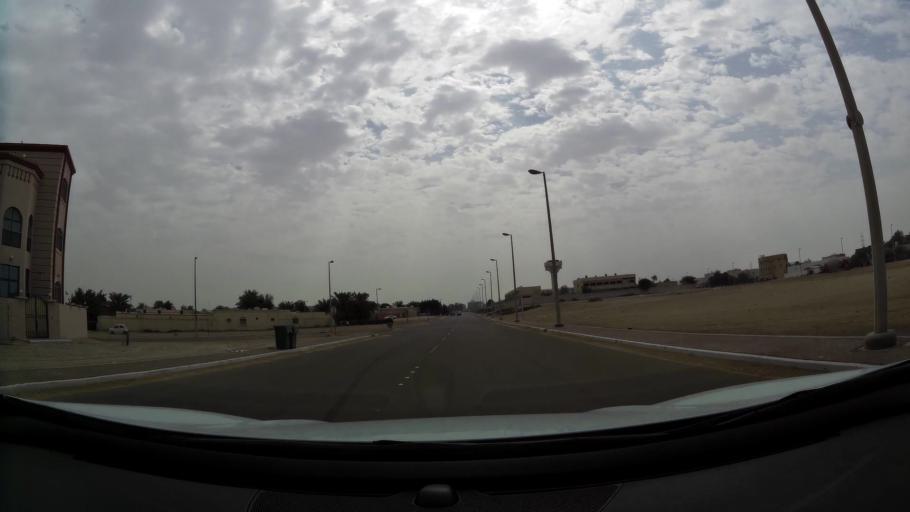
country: AE
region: Abu Dhabi
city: Abu Dhabi
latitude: 24.3176
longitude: 54.6423
